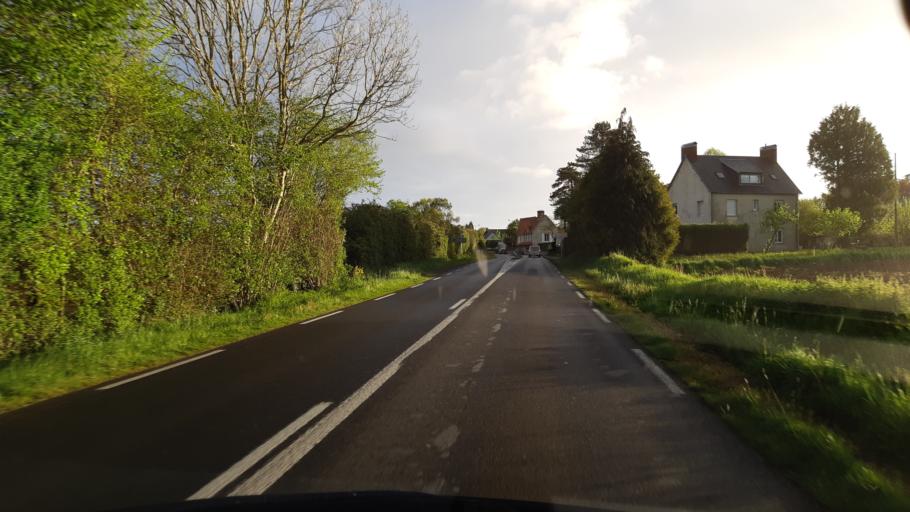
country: FR
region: Lower Normandy
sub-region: Departement de la Manche
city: Agneaux
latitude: 49.0437
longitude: -1.1289
